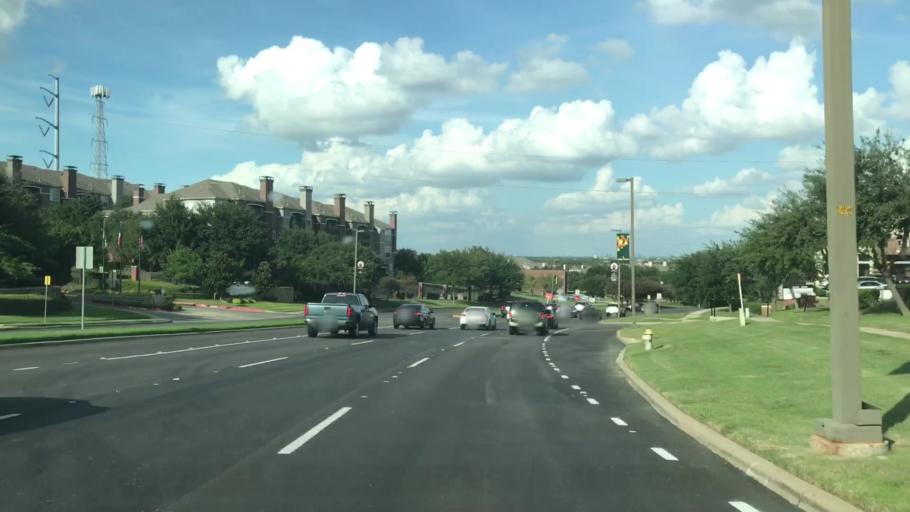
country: US
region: Texas
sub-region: Dallas County
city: Farmers Branch
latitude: 32.9213
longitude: -96.9582
